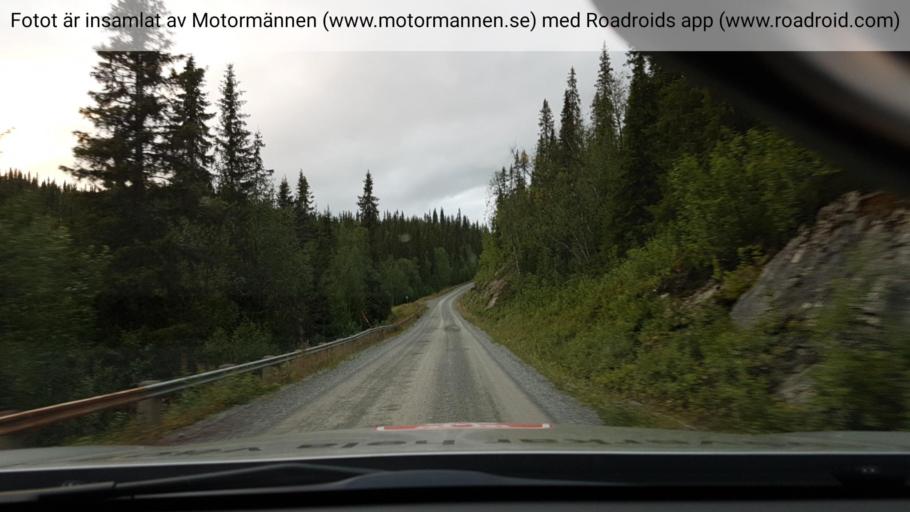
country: SE
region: Vaesterbotten
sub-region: Vilhelmina Kommun
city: Sjoberg
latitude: 65.5318
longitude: 15.4357
